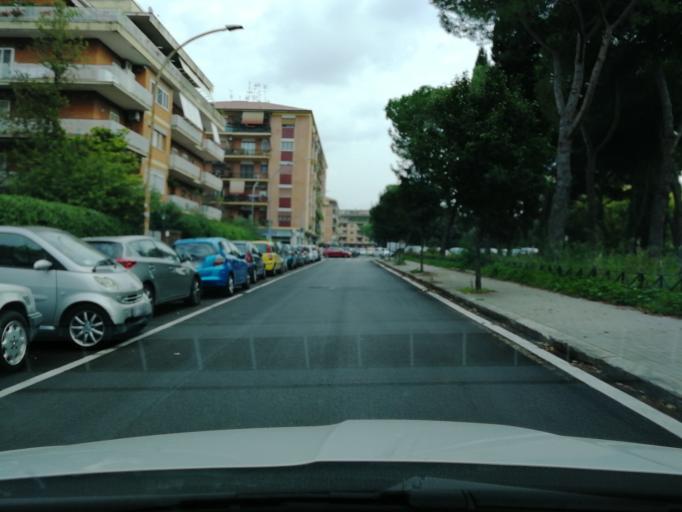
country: IT
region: Latium
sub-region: Citta metropolitana di Roma Capitale
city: Rome
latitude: 41.8540
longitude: 12.5569
